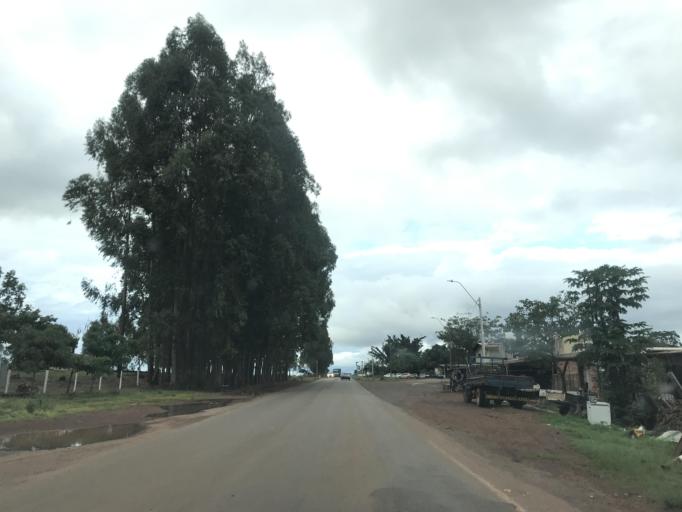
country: BR
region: Goias
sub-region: Luziania
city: Luziania
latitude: -16.4628
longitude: -48.2128
